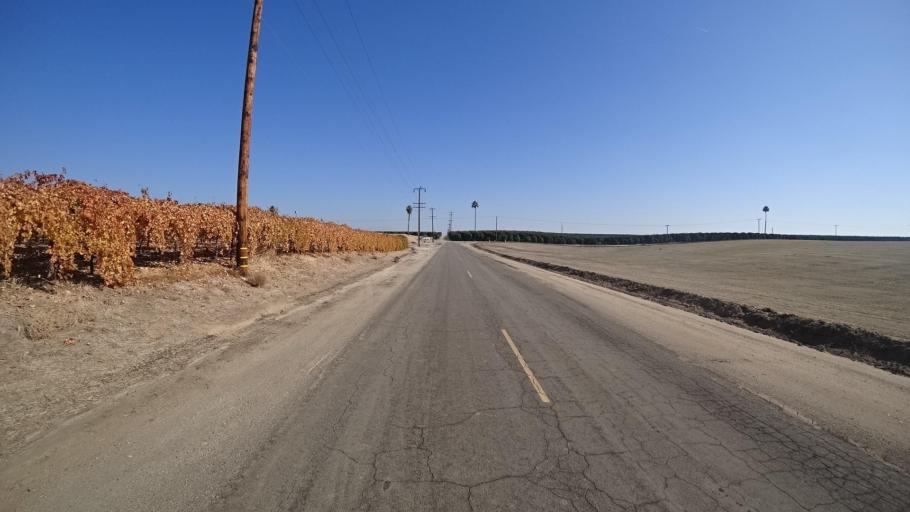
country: US
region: California
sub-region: Kern County
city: McFarland
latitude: 35.7036
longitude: -119.1356
